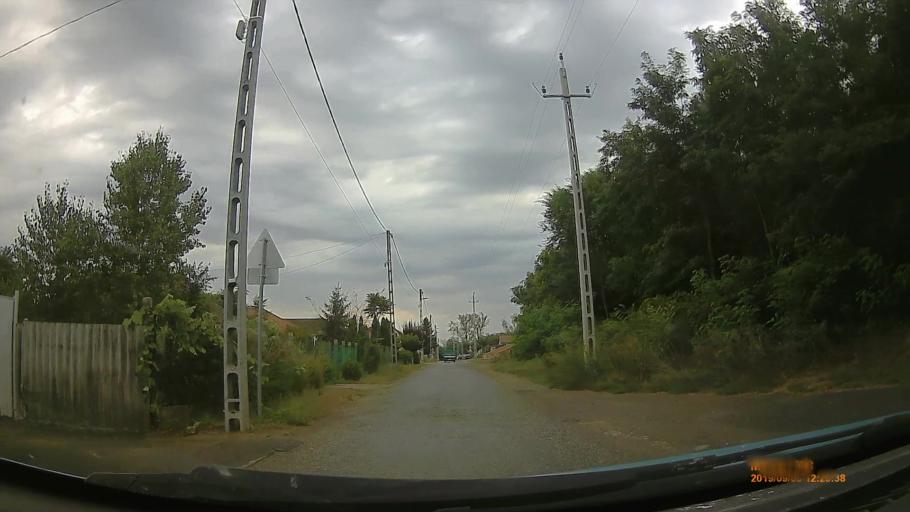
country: HU
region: Szabolcs-Szatmar-Bereg
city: Nyirpazony
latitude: 48.0100
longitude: 21.8248
